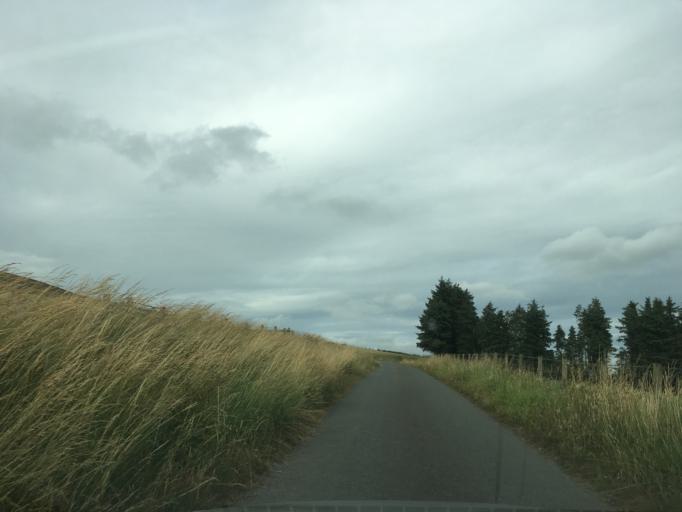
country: GB
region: Scotland
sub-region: South Lanarkshire
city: Douglas
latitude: 55.5172
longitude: -3.7090
